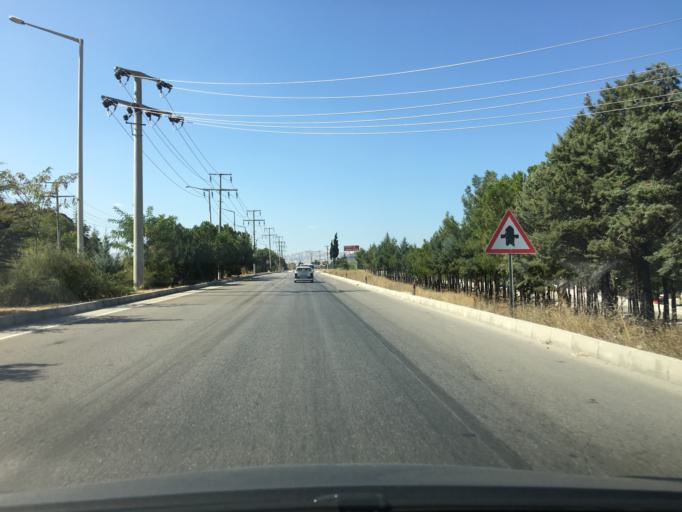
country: TR
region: Burdur
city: Burdur
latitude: 37.7447
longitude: 30.3169
